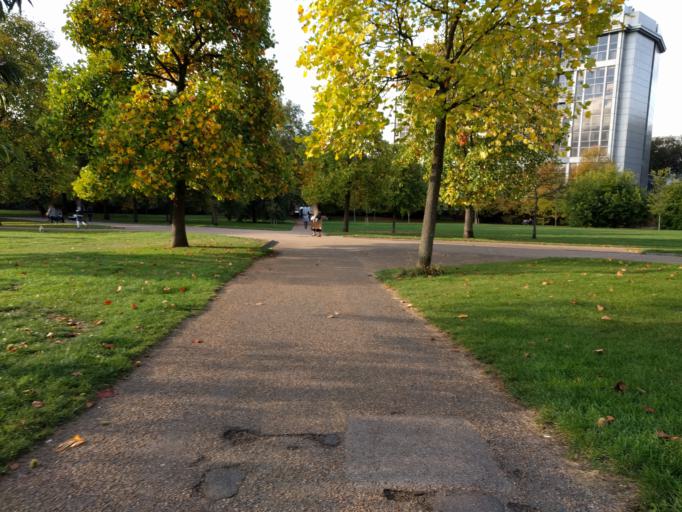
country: GB
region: England
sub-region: Greater London
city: Kensington
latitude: 51.5036
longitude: -0.1866
